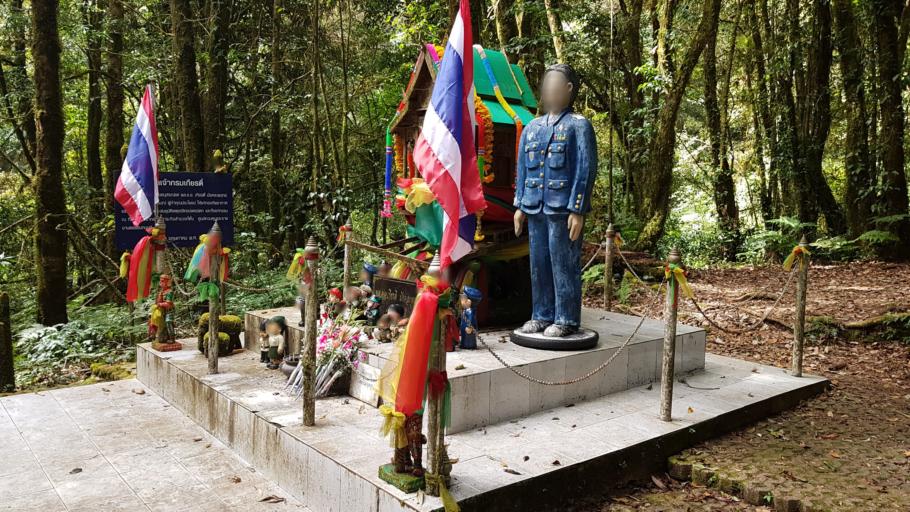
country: TH
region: Chiang Mai
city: Mae Chaem
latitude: 18.5888
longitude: 98.4844
